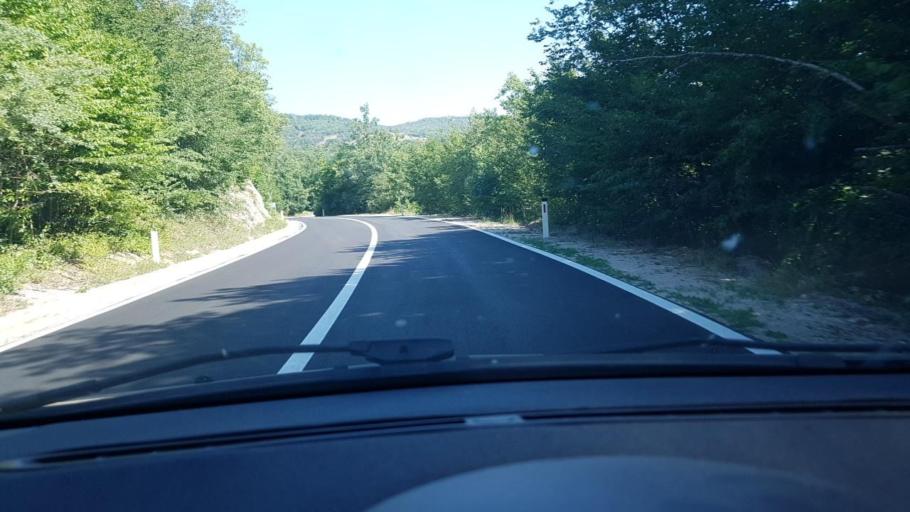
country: BA
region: Federation of Bosnia and Herzegovina
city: Bosansko Grahovo
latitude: 44.3085
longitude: 16.3084
